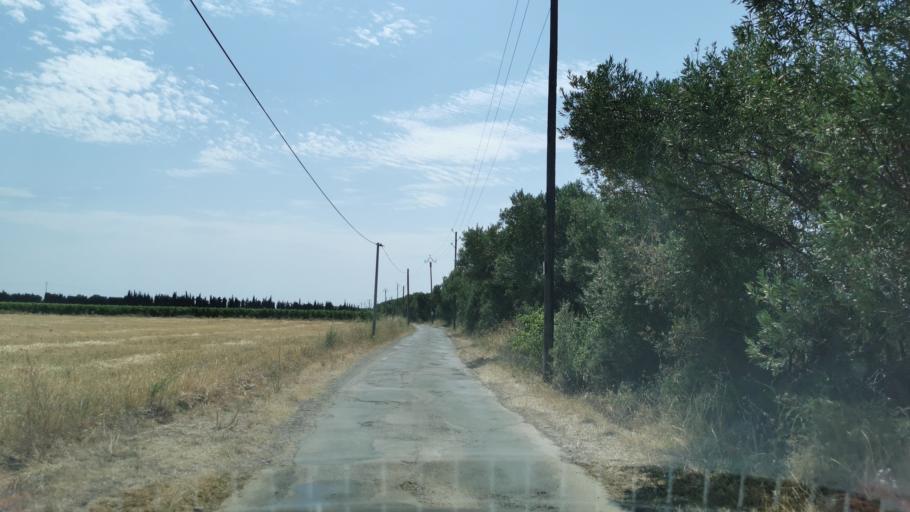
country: FR
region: Languedoc-Roussillon
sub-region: Departement de l'Aude
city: Bize-Minervois
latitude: 43.2933
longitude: 2.8847
